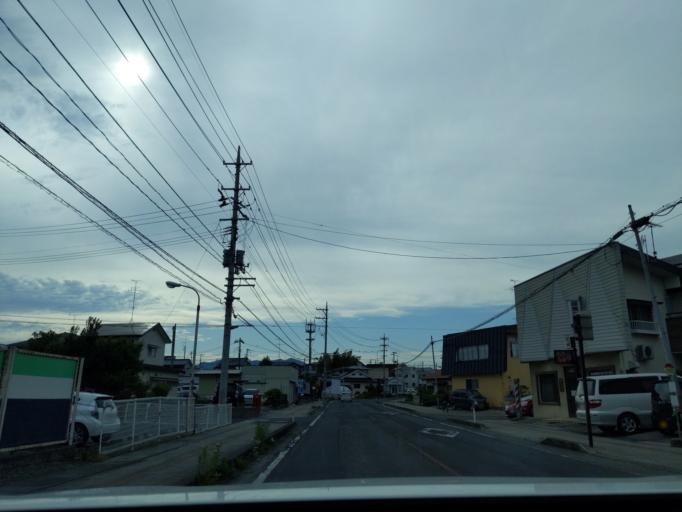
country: JP
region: Fukushima
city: Koriyama
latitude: 37.4109
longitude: 140.3353
